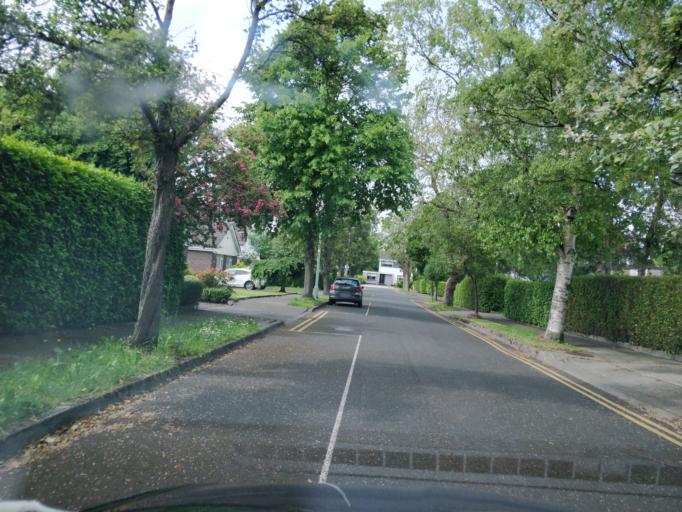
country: IE
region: Leinster
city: Dundrum
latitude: 53.2852
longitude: -6.2484
